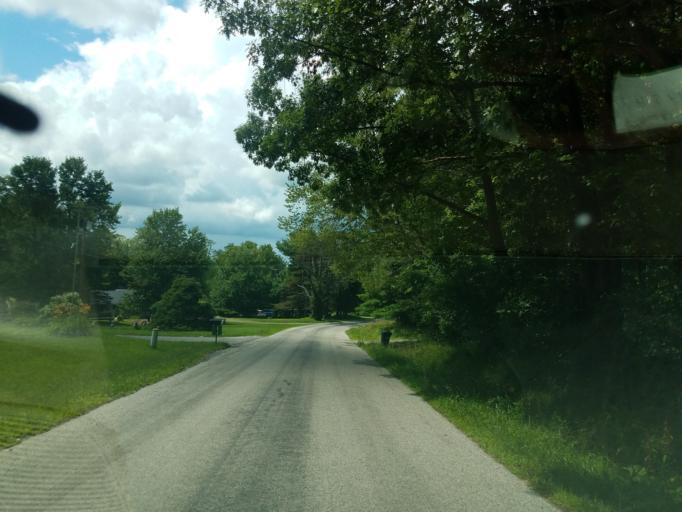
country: US
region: Ohio
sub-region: Richland County
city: Lincoln Heights
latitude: 40.8469
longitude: -82.4627
